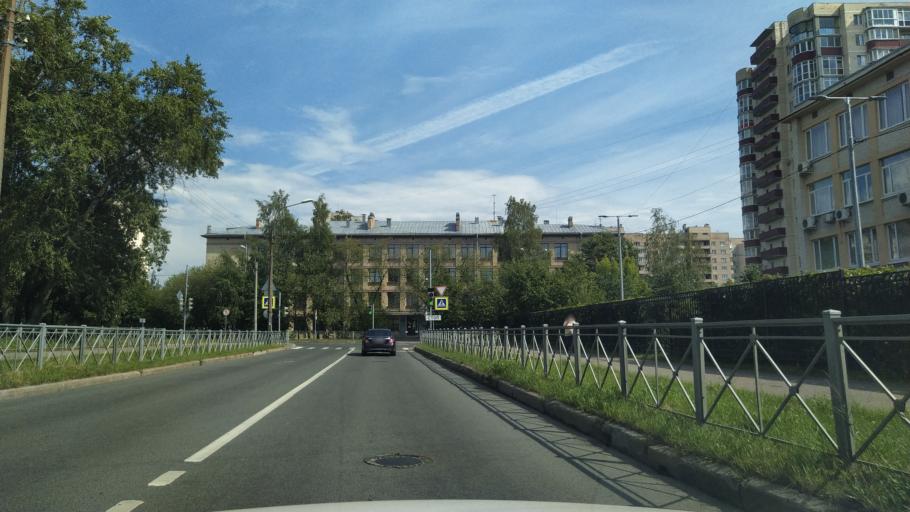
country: RU
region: Leningrad
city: Kalininskiy
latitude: 59.9995
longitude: 30.3778
